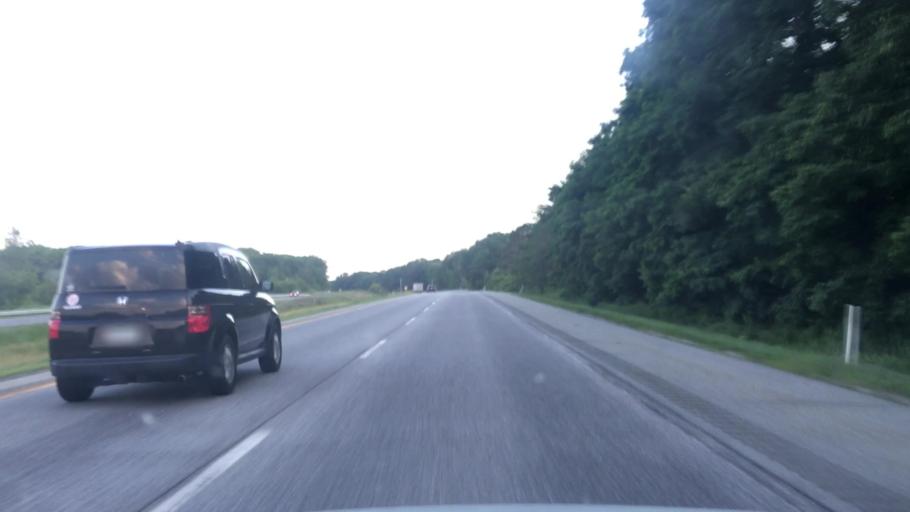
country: US
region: Maine
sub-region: Cumberland County
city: Falmouth
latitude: 43.6977
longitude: -70.2567
